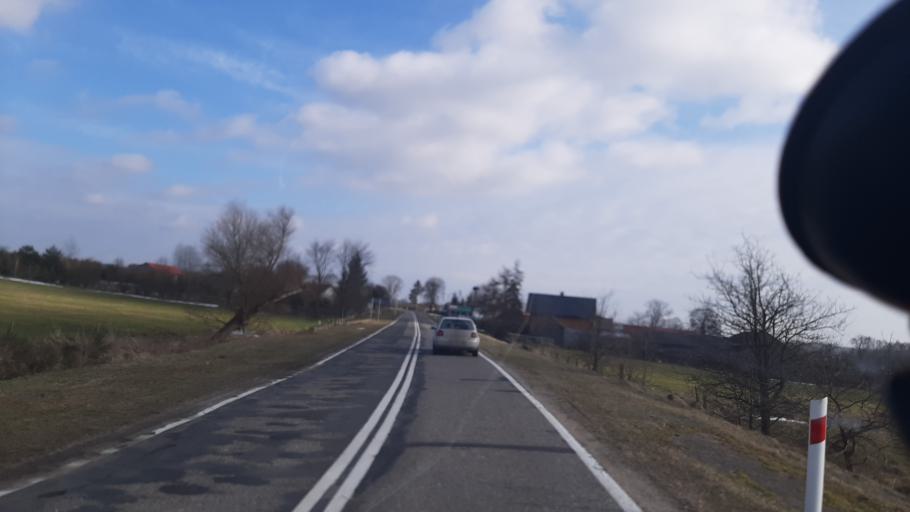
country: PL
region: Lublin Voivodeship
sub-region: Powiat parczewski
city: Sosnowica
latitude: 51.5003
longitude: 23.1472
